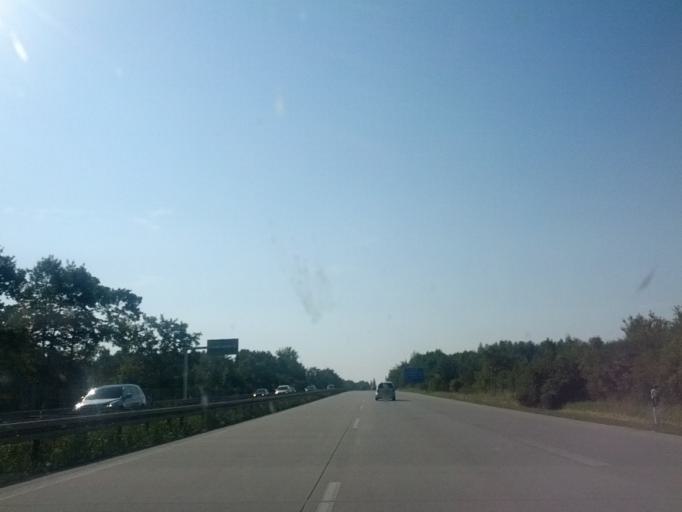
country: DE
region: Brandenburg
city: Bernau bei Berlin
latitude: 52.6888
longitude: 13.5594
